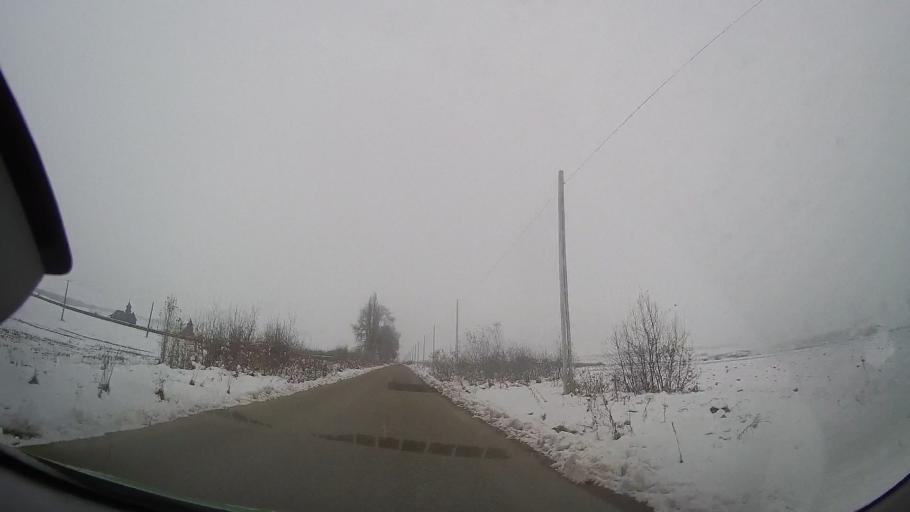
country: RO
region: Vaslui
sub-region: Comuna Todiresti
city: Todiresti
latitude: 46.8474
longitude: 27.3957
